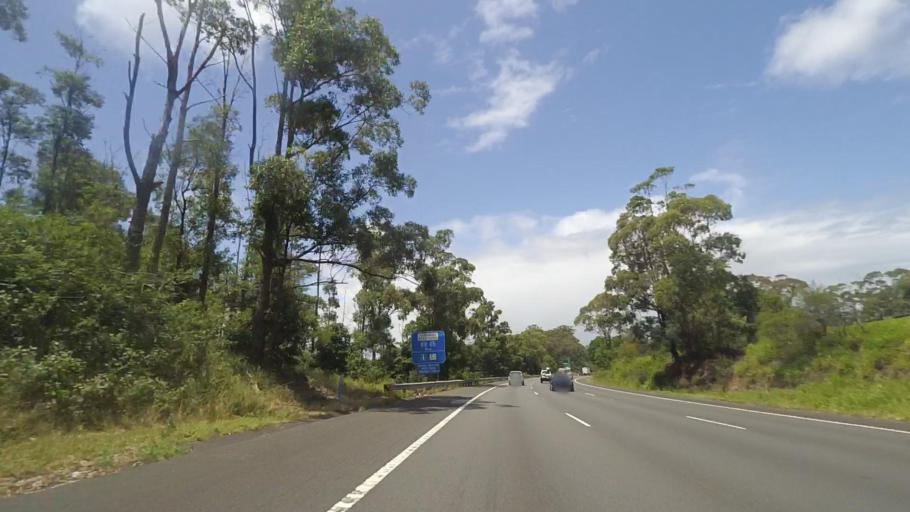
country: AU
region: New South Wales
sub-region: Gosford Shire
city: Lisarow
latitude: -33.3570
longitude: 151.3456
